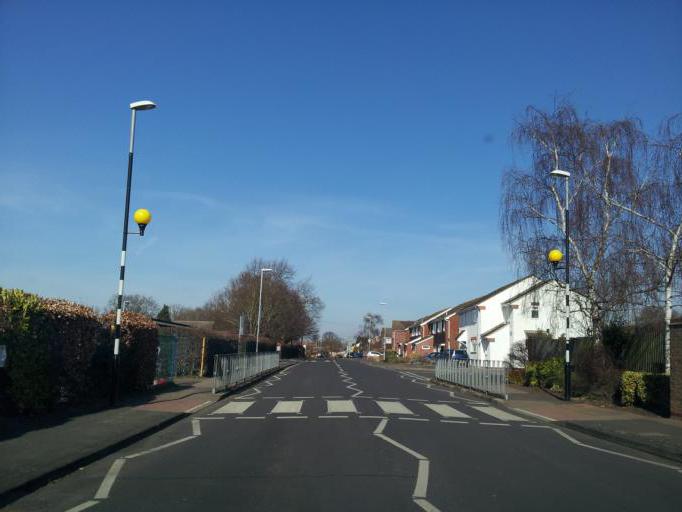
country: GB
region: England
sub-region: Cambridgeshire
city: Little Paxton
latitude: 52.2465
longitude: -0.2590
